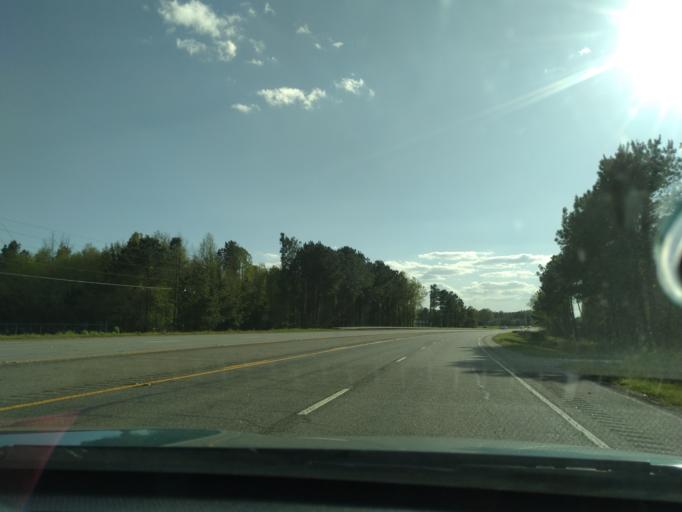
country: US
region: South Carolina
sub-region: Williamsburg County
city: Kingstree
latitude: 33.6407
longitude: -79.9007
